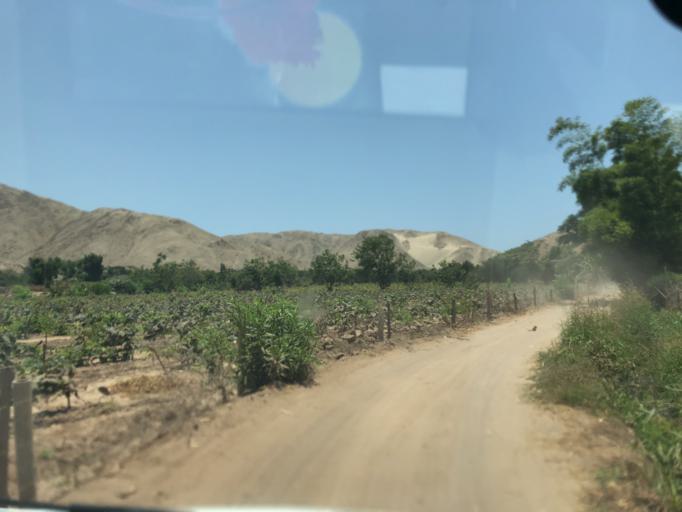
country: PE
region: Lima
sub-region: Provincia de Canete
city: Quilmana
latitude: -12.9951
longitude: -76.4403
